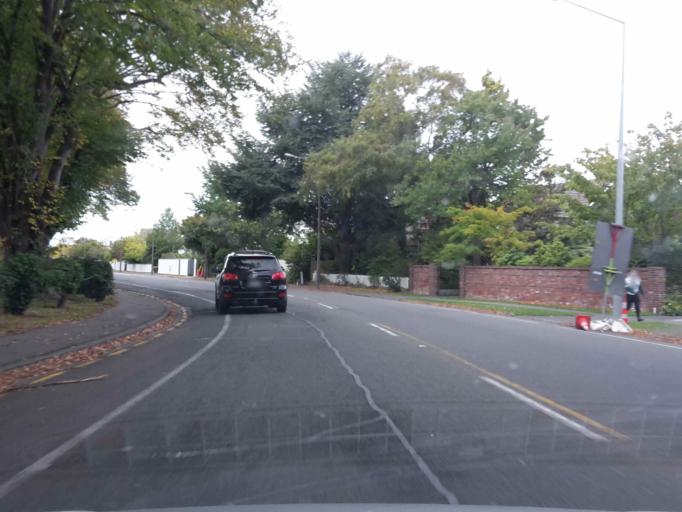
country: NZ
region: Canterbury
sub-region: Christchurch City
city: Christchurch
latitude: -43.5130
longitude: 172.6109
